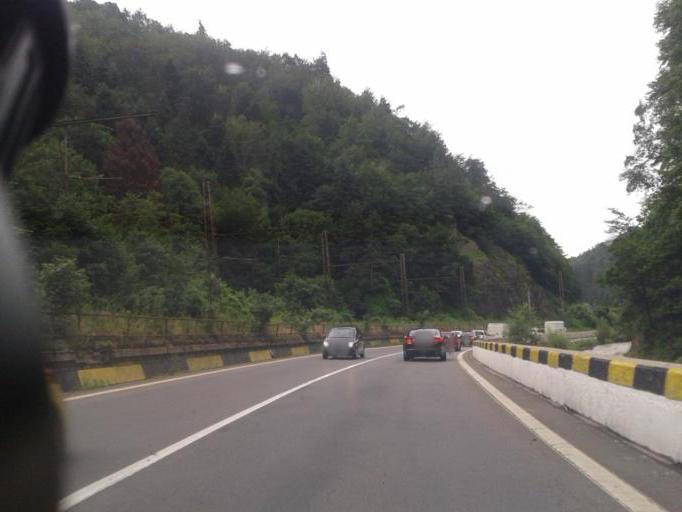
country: RO
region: Brasov
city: Brasov
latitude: 45.5710
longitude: 25.6094
